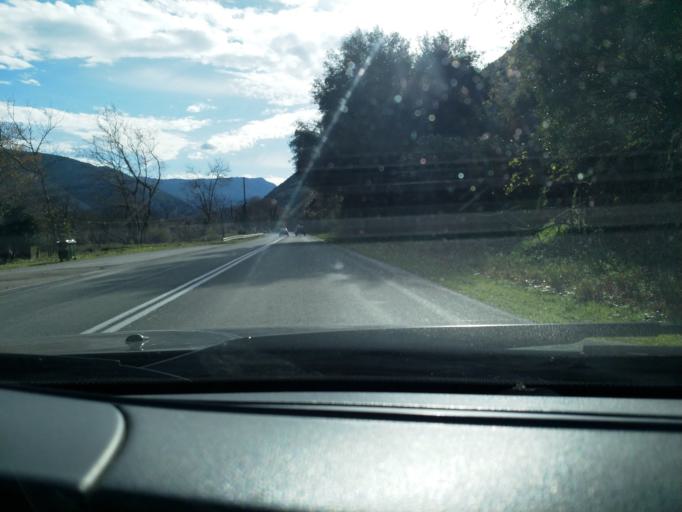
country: GR
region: Epirus
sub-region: Nomos Prevezis
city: Pappadates
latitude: 39.3863
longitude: 20.8671
